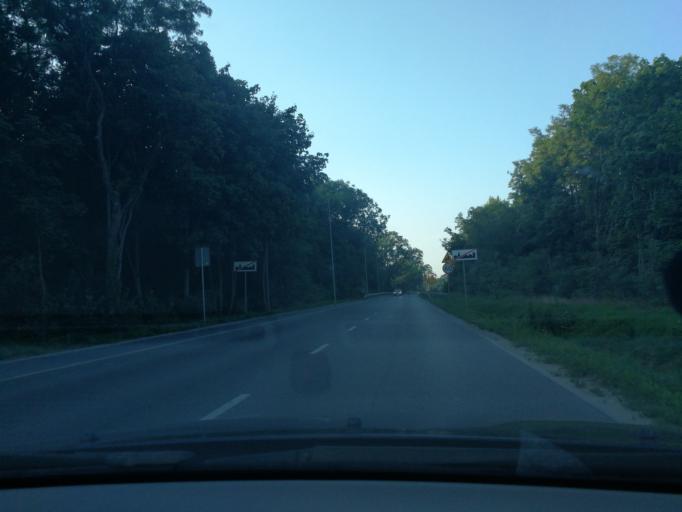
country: PL
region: Masovian Voivodeship
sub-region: Powiat pruszkowski
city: Brwinow
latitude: 52.1820
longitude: 20.7502
